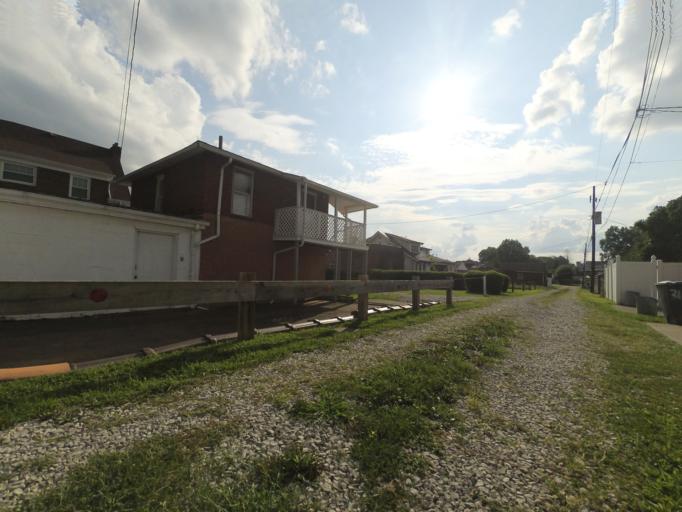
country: US
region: West Virginia
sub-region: Cabell County
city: Huntington
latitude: 38.4309
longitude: -82.3928
